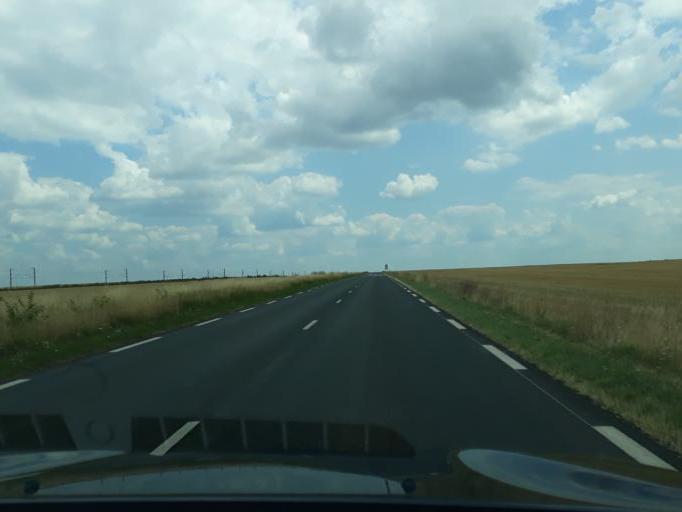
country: FR
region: Centre
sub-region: Departement du Cher
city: Avord
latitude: 47.0156
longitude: 2.7139
